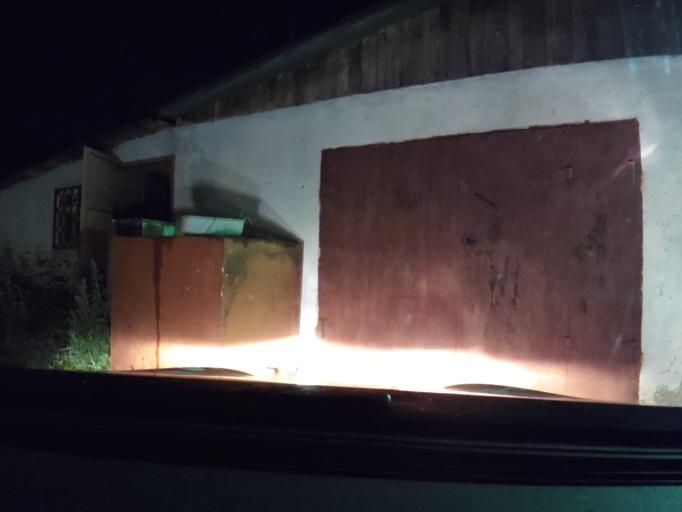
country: RU
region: Chelyabinsk
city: Sim
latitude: 55.0052
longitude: 57.7079
